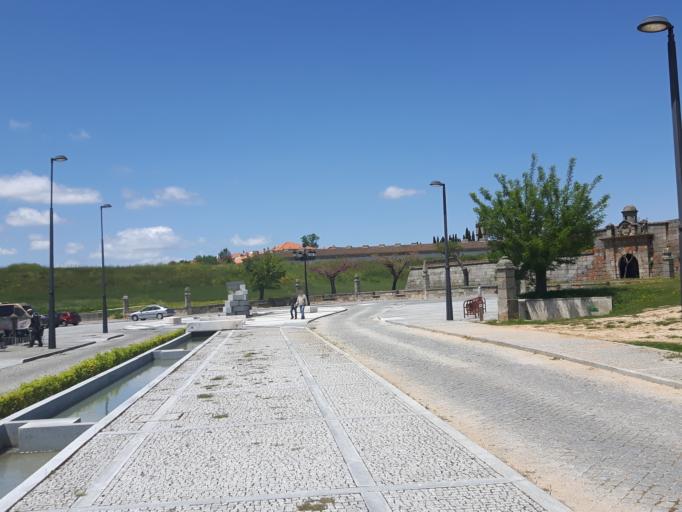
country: ES
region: Castille and Leon
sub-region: Provincia de Salamanca
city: Aldea del Obispo
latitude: 40.7226
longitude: -6.9041
